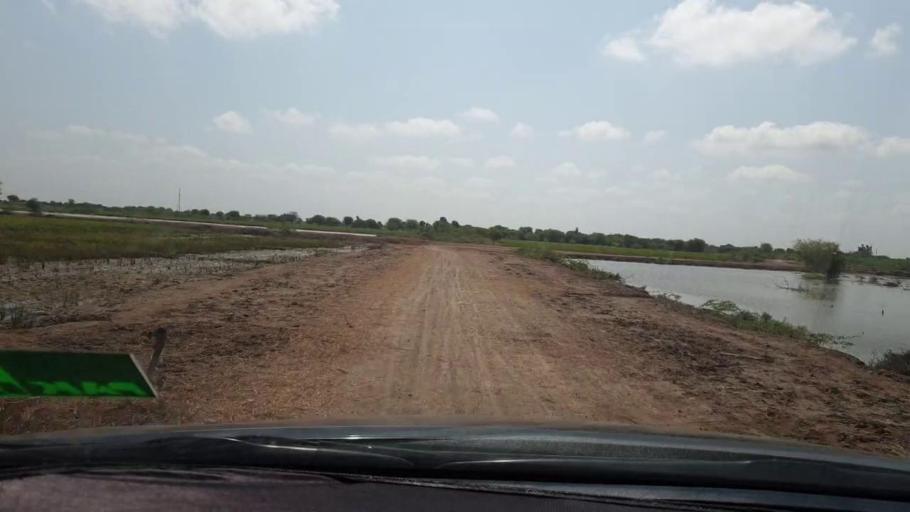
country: PK
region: Sindh
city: Tando Bago
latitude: 24.9347
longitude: 69.0946
